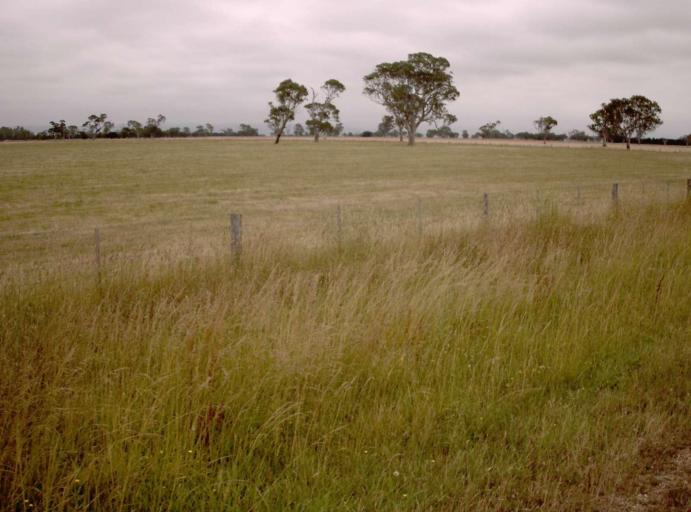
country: AU
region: Victoria
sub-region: Wellington
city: Heyfield
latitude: -38.0598
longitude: 146.7691
